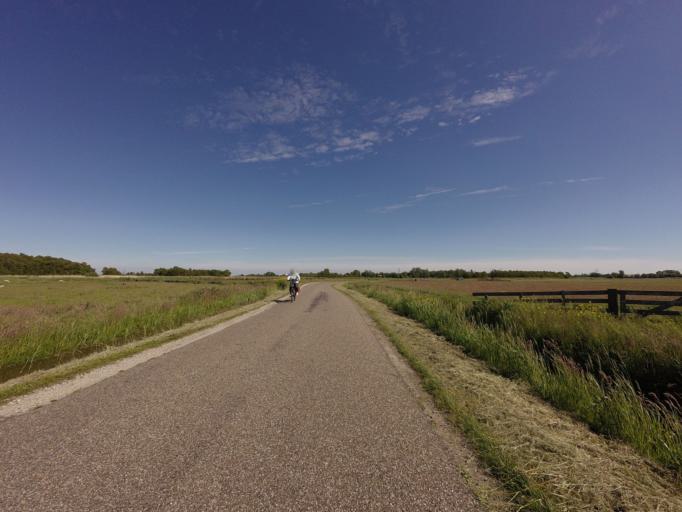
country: NL
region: North Holland
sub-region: Gemeente Uitgeest
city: Uitgeest
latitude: 52.5237
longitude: 4.7468
